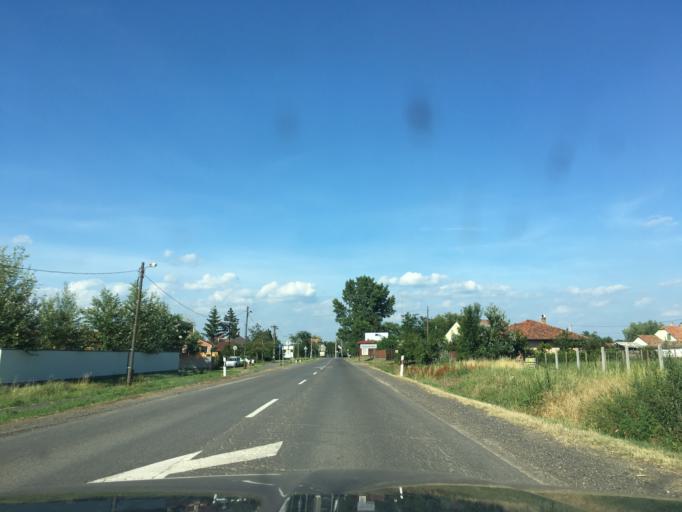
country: HU
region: Hajdu-Bihar
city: Hajdusamson
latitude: 47.5949
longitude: 21.7397
